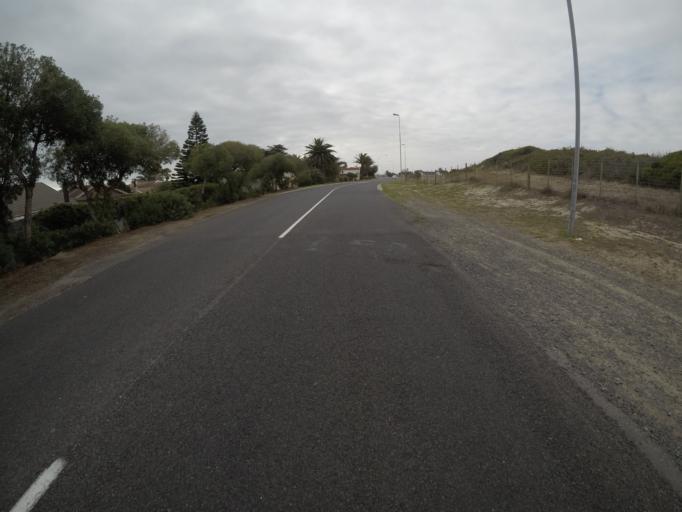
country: ZA
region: Western Cape
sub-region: City of Cape Town
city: Atlantis
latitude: -33.6977
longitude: 18.4444
